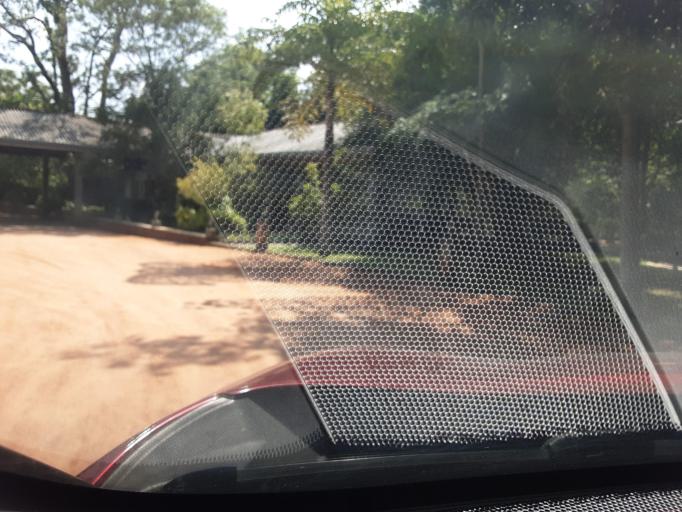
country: LK
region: Central
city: Sigiriya
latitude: 8.0013
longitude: 80.7474
